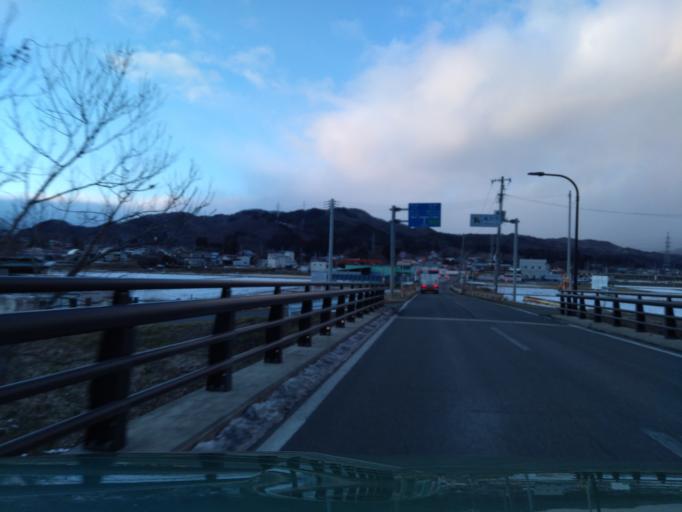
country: JP
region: Iwate
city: Shizukuishi
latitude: 39.6974
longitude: 141.0635
